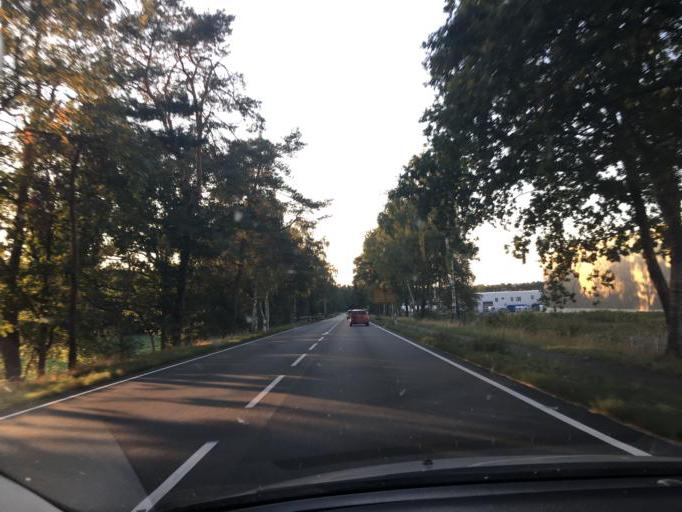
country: DE
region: Lower Saxony
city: Soltau
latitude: 52.9417
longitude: 9.8847
